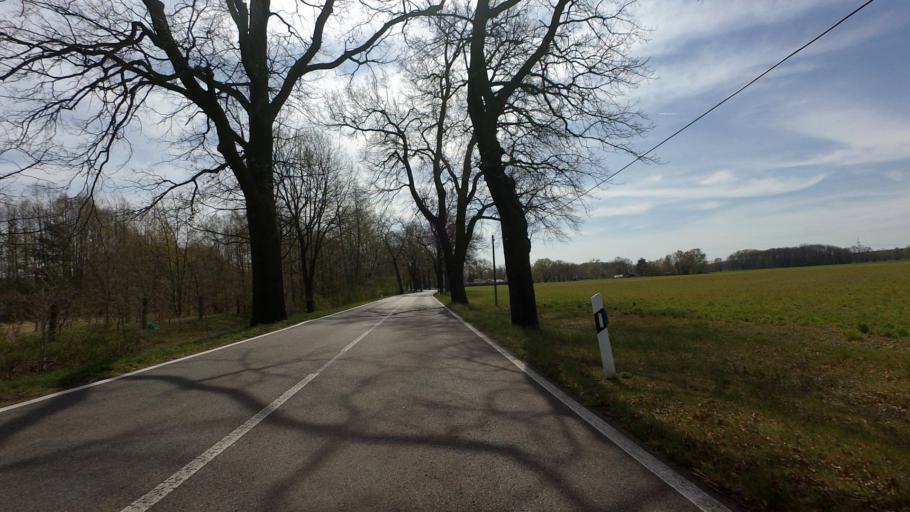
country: DE
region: Brandenburg
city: Trebbin
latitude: 52.2584
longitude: 13.2047
